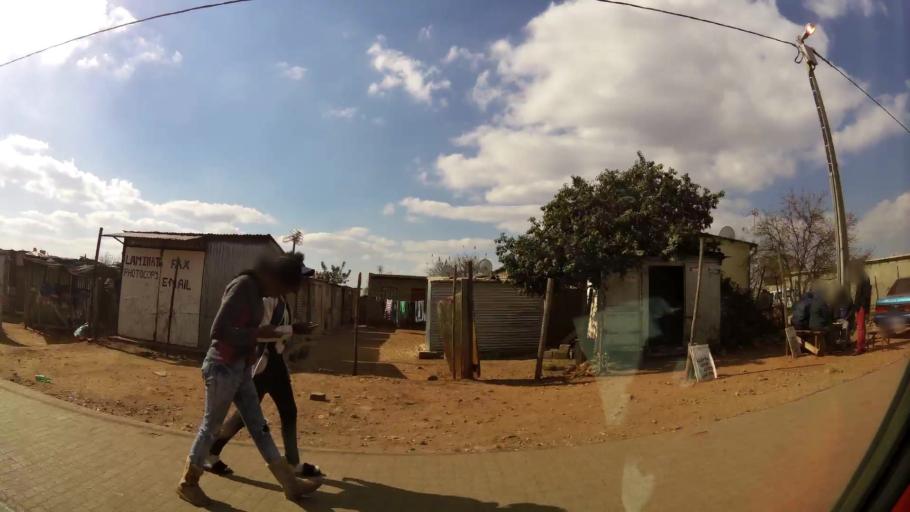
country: ZA
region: Gauteng
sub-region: Ekurhuleni Metropolitan Municipality
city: Tembisa
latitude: -25.9866
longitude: 28.2250
